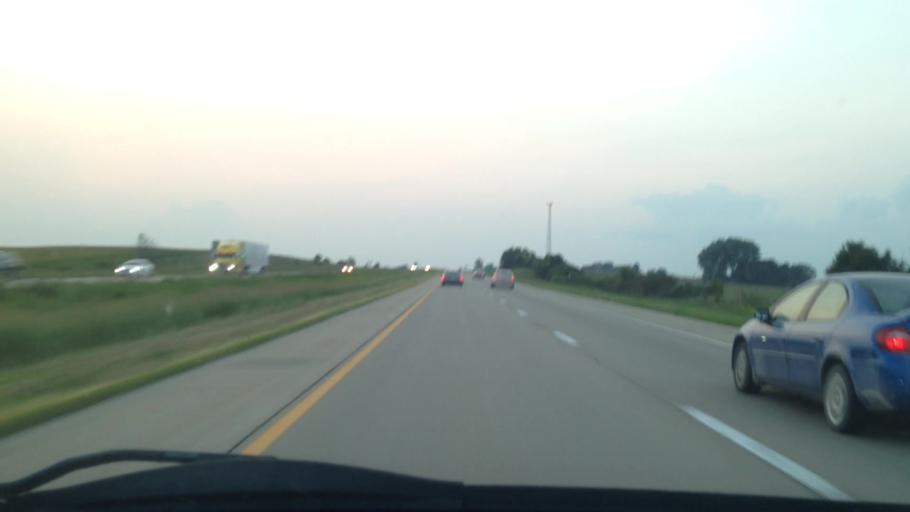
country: US
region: Iowa
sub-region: Benton County
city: Urbana
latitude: 42.3037
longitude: -91.9673
